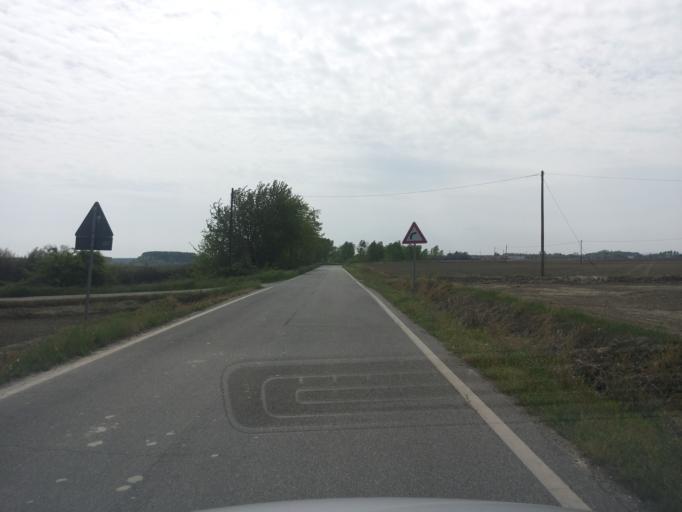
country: IT
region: Piedmont
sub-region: Provincia di Vercelli
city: Motta De Conti
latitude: 45.2063
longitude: 8.5147
